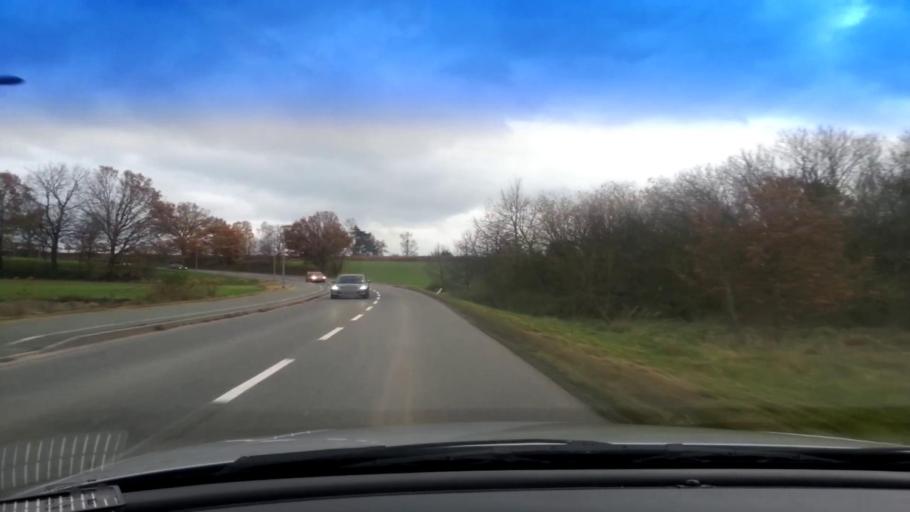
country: DE
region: Bavaria
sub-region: Upper Franconia
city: Stegaurach
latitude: 49.8726
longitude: 10.8664
